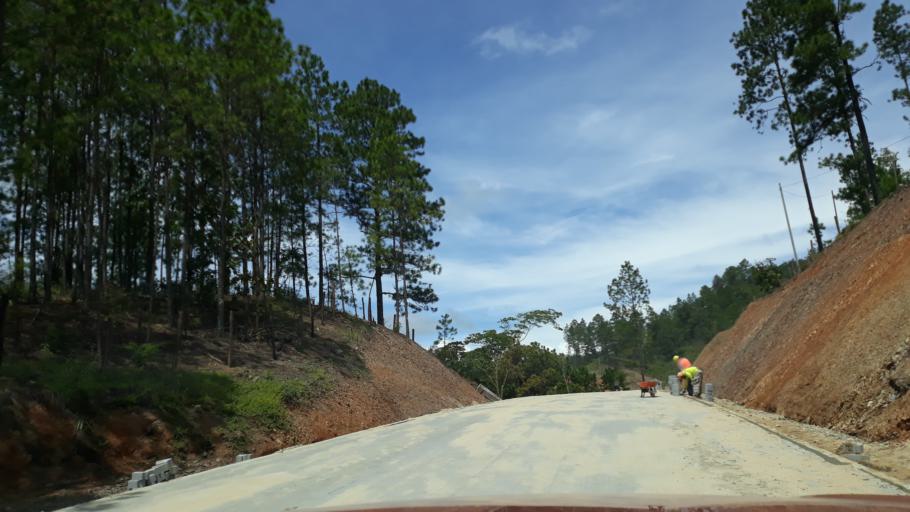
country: HN
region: El Paraiso
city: Santa Cruz
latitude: 13.7582
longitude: -86.6320
